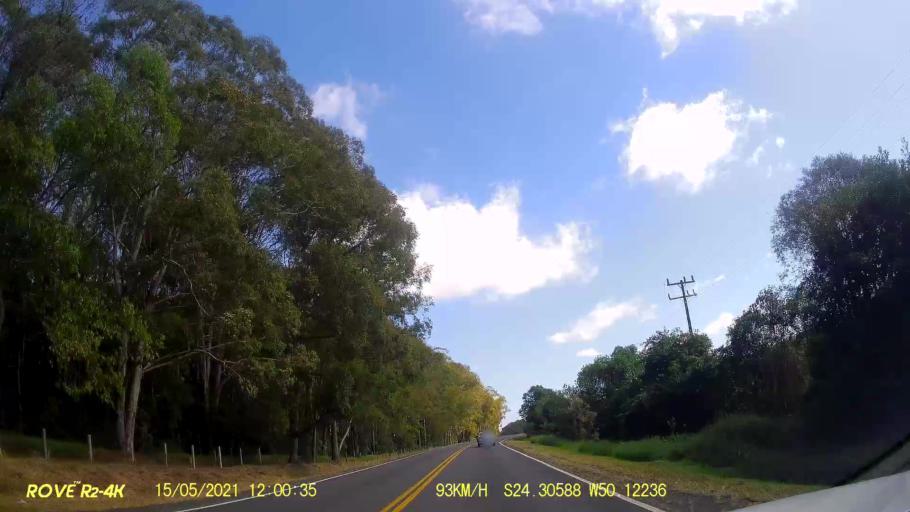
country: BR
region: Parana
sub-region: Pirai Do Sul
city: Pirai do Sul
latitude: -24.3059
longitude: -50.1222
